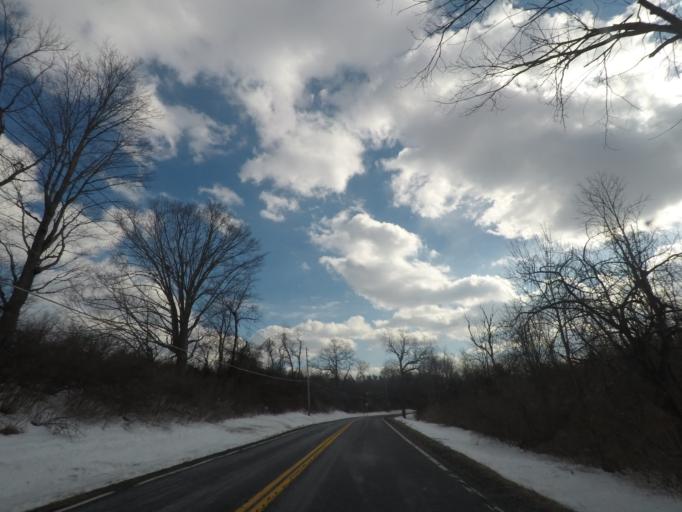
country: US
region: New York
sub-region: Schenectady County
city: Niskayuna
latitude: 42.8195
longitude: -73.8503
